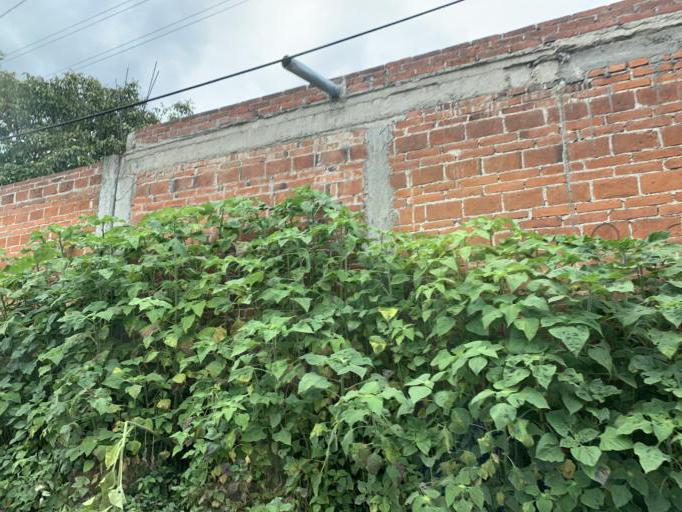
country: MX
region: Puebla
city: Huejotzingo
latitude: 19.1507
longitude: -98.4020
